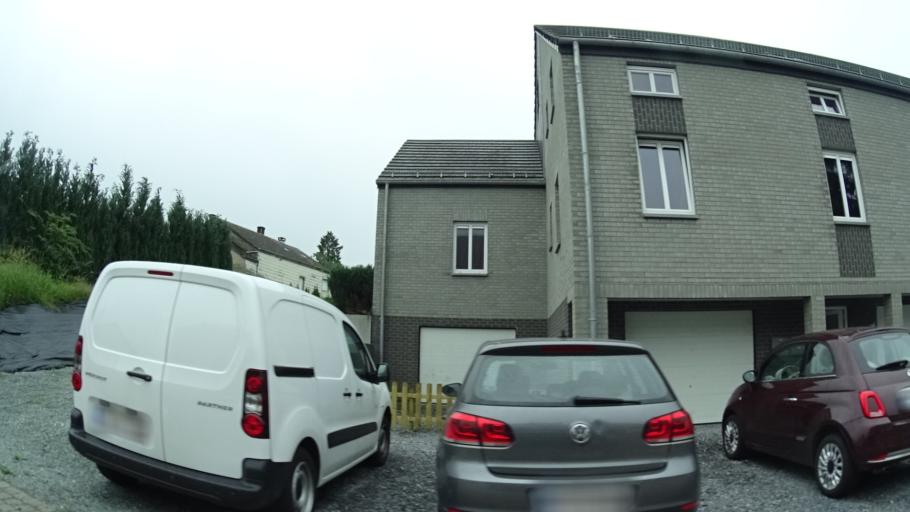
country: BE
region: Wallonia
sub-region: Province du Luxembourg
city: Neufchateau
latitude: 49.9020
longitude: 5.3529
